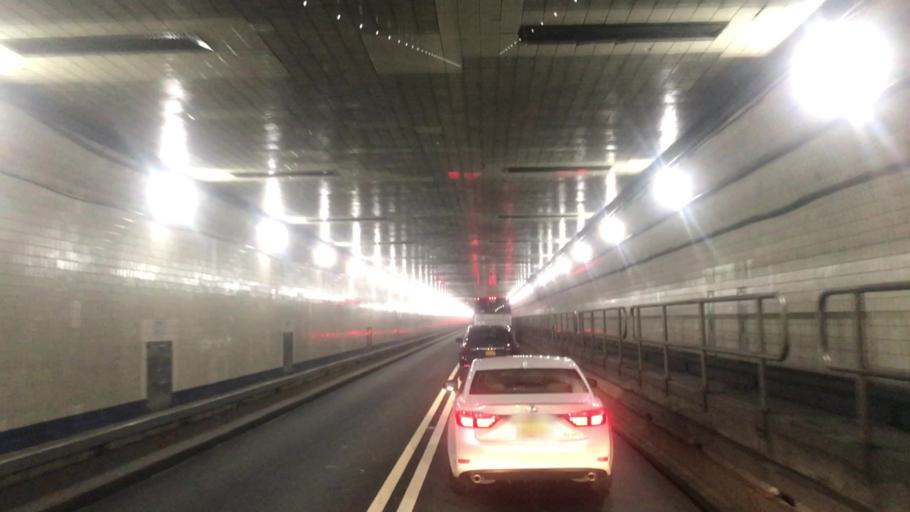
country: US
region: New Jersey
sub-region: Hudson County
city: Weehawken
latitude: 40.7629
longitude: -74.0172
